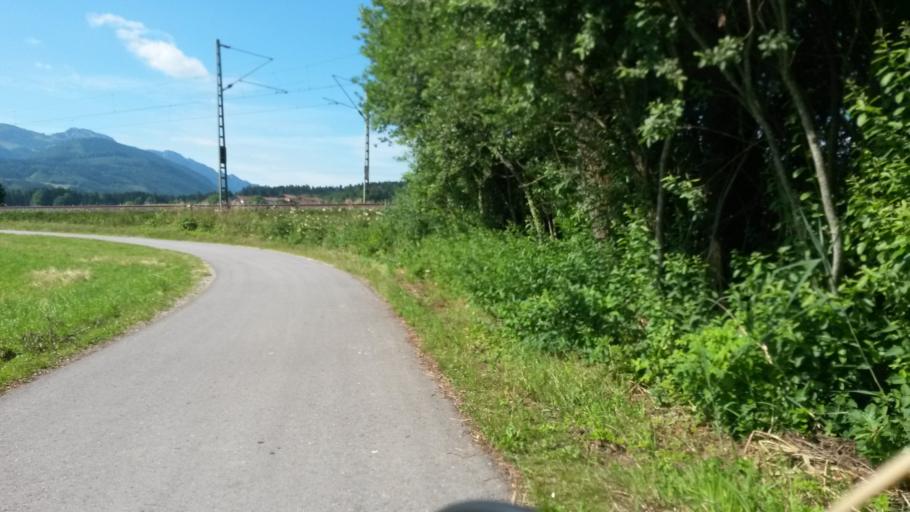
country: DE
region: Bavaria
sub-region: Upper Bavaria
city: Bernau am Chiemsee
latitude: 47.8282
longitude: 12.3614
